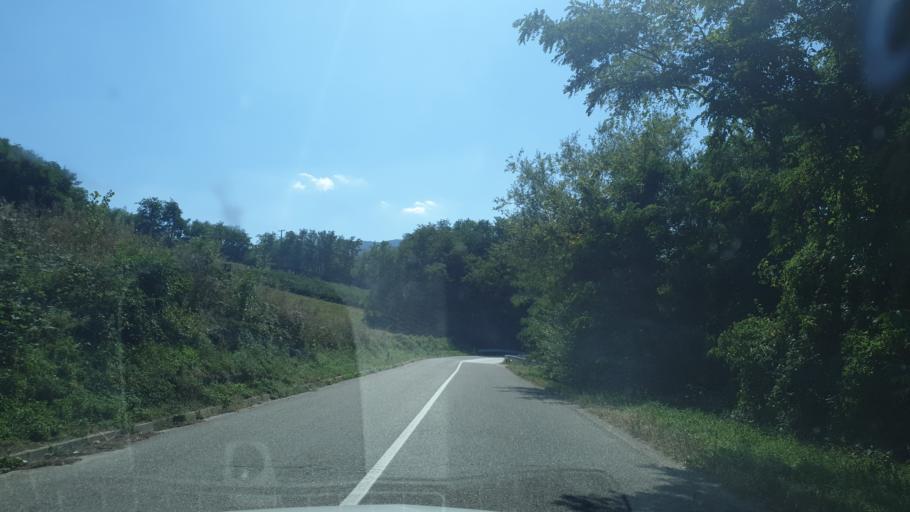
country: RS
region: Central Serbia
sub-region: Kolubarski Okrug
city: Mionica
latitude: 44.1753
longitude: 20.0198
